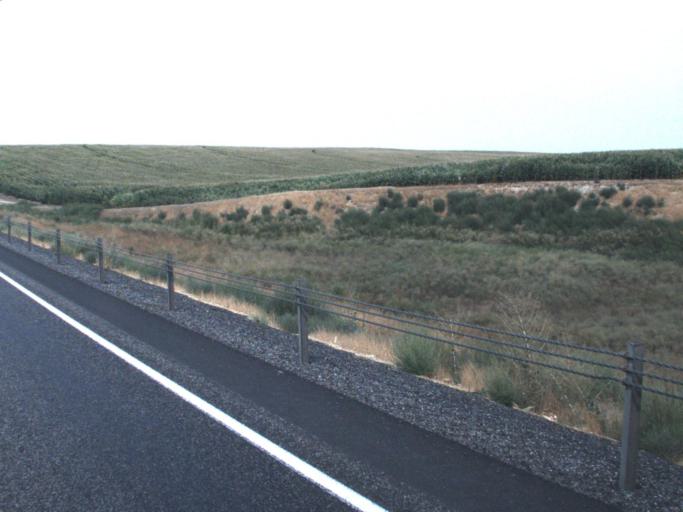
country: US
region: Oregon
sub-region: Morrow County
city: Irrigon
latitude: 46.0678
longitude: -119.6021
